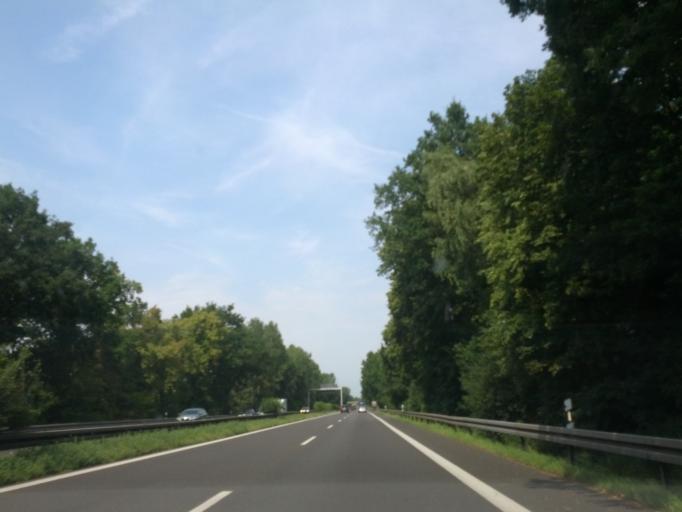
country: DE
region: Brandenburg
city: Gross Kreutz
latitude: 52.3624
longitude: 12.8153
